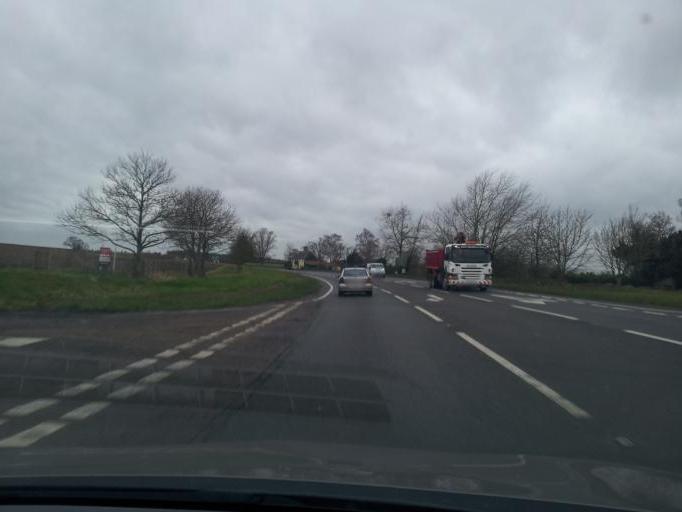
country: GB
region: England
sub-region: Suffolk
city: Ixworth
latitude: 52.2926
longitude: 0.8295
